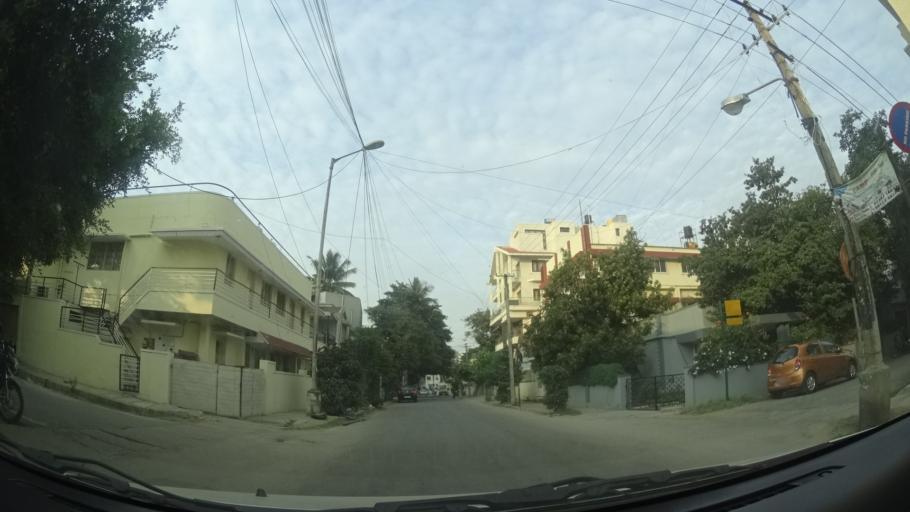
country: IN
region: Karnataka
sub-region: Bangalore Urban
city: Bangalore
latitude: 13.0026
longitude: 77.6264
